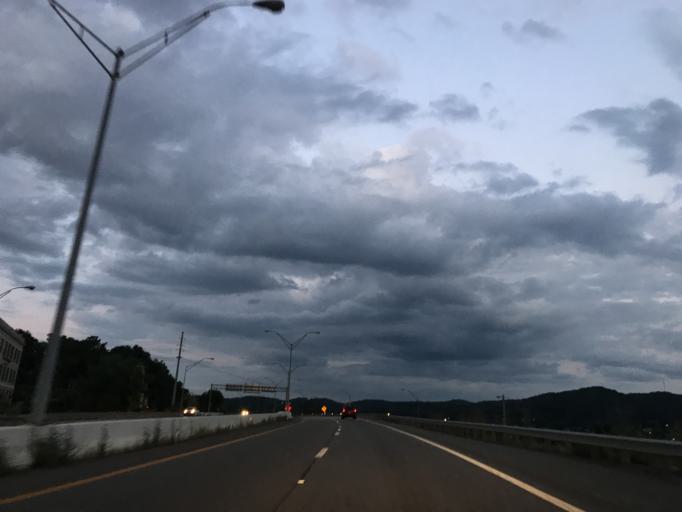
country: US
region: Ohio
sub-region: Columbiana County
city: East Liverpool
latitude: 40.6163
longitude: -80.5783
